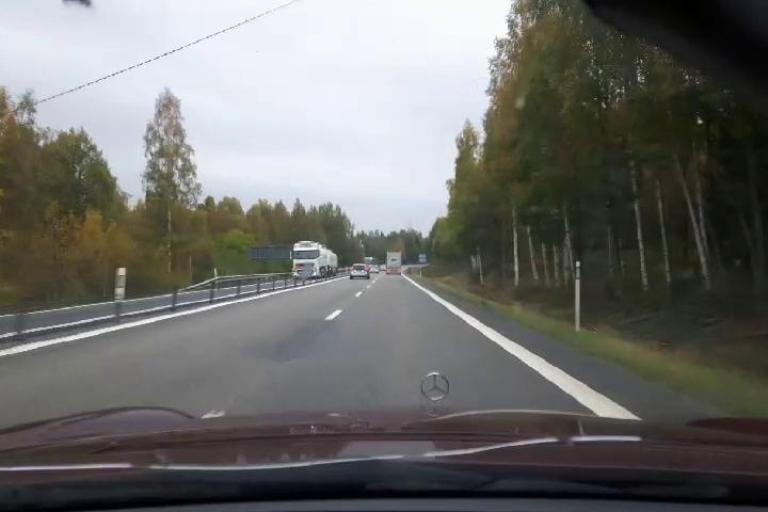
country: SE
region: Vaesternorrland
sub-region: Kramfors Kommun
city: Nordingra
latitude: 63.0615
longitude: 18.3528
